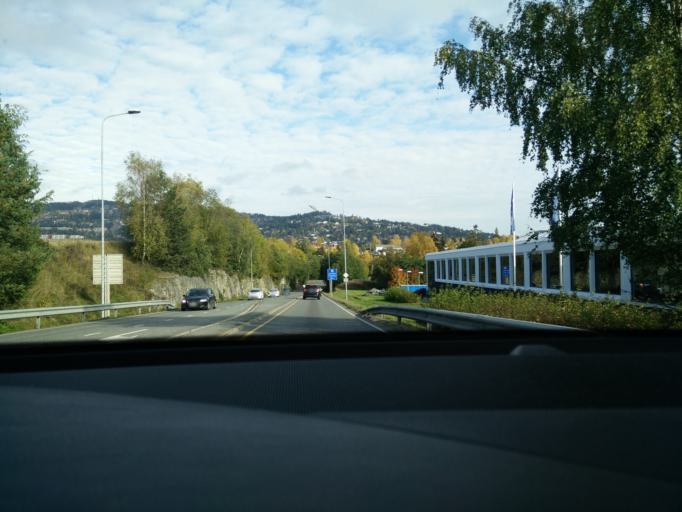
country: NO
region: Akershus
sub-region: Baerum
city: Lysaker
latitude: 59.9511
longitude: 10.6285
